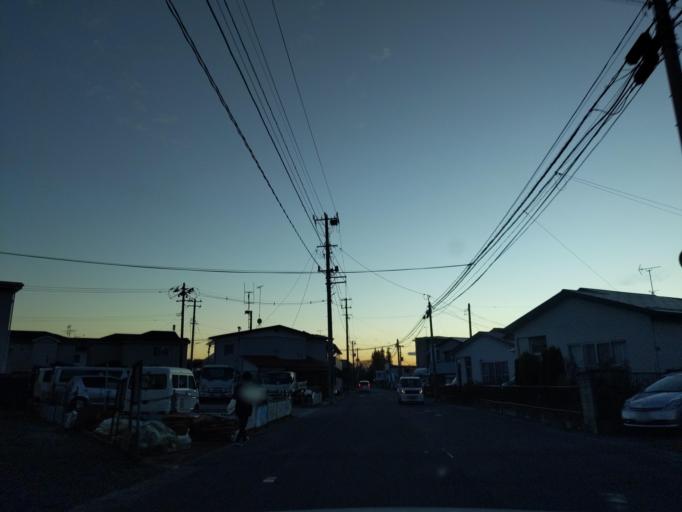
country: JP
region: Fukushima
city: Koriyama
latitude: 37.3628
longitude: 140.3902
